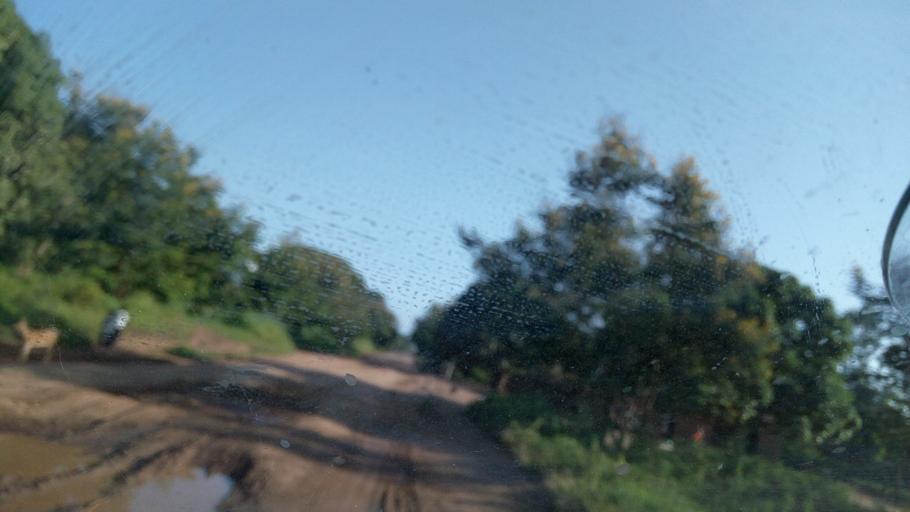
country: BI
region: Bururi
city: Rumonge
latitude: -4.0672
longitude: 29.0881
